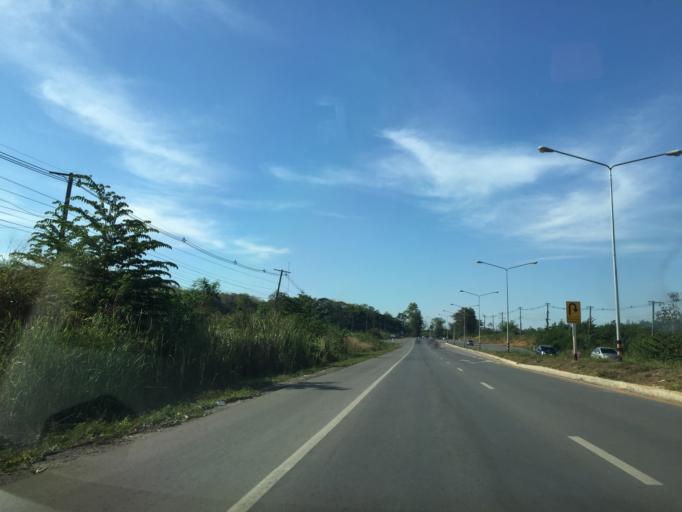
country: TH
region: Loei
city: Wang Saphung
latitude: 17.2969
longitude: 101.8139
